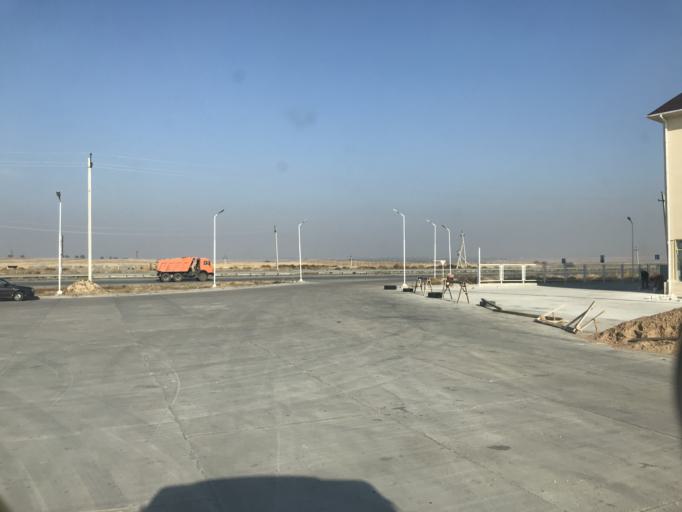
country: KZ
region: Ongtustik Qazaqstan
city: Shymkent
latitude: 42.4494
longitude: 69.6424
